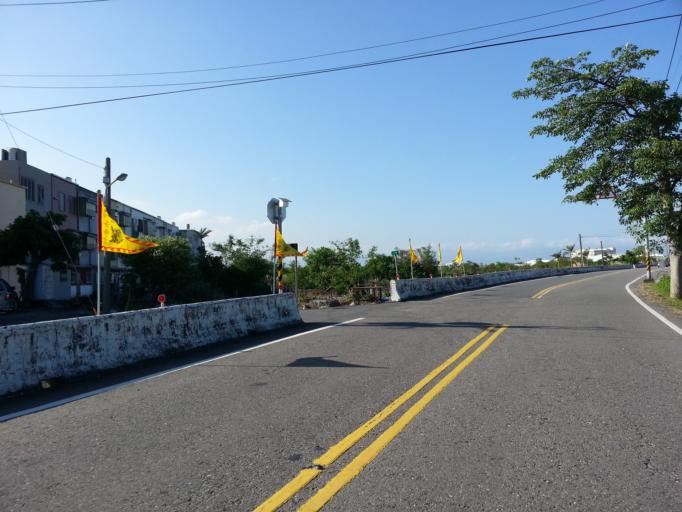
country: TW
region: Taiwan
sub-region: Yilan
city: Yilan
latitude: 24.6258
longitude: 121.8335
